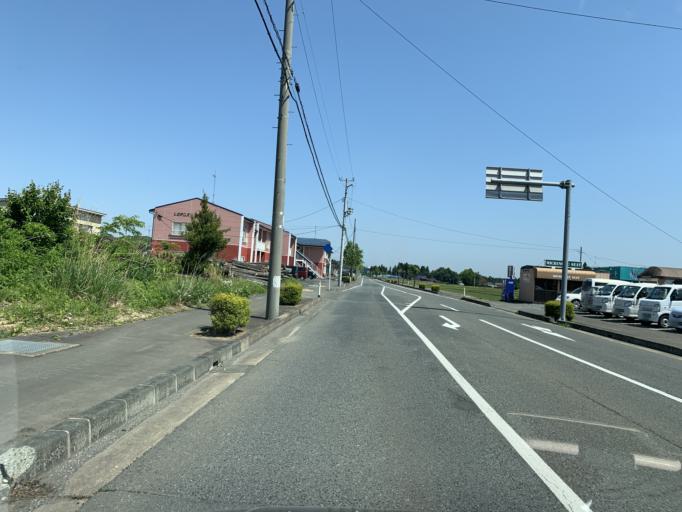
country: JP
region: Iwate
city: Mizusawa
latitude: 39.1964
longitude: 141.0952
